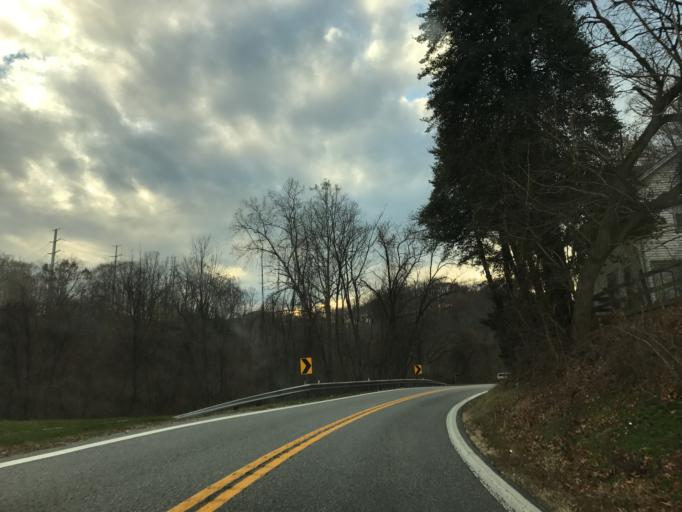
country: US
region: Maryland
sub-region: Baltimore County
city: Perry Hall
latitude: 39.4217
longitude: -76.4969
